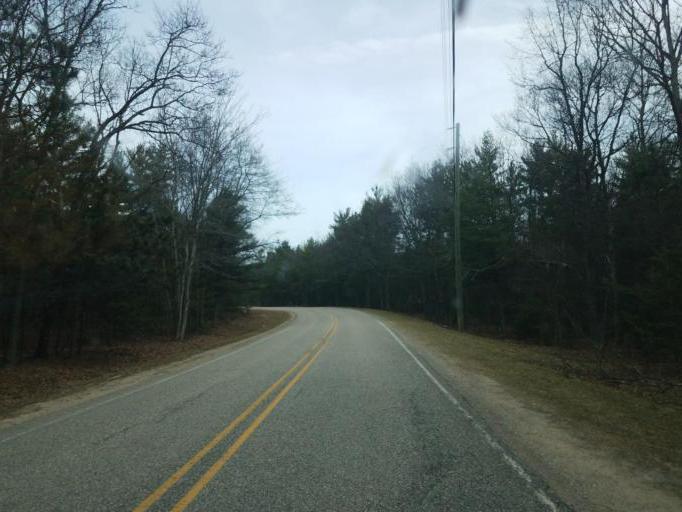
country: US
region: Michigan
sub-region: Oceana County
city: Hart
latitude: 43.7609
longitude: -86.4425
